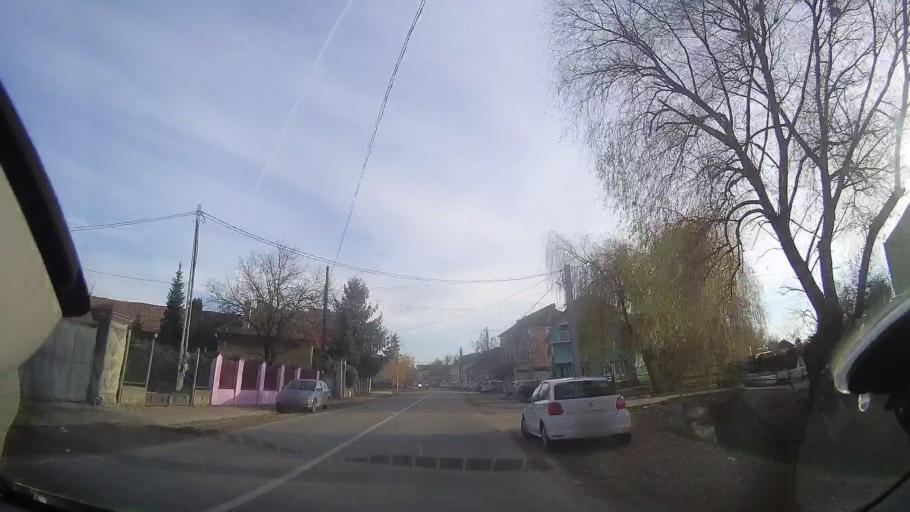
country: RO
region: Bihor
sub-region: Comuna Tileagd
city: Tileagd
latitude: 47.0727
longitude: 22.1968
